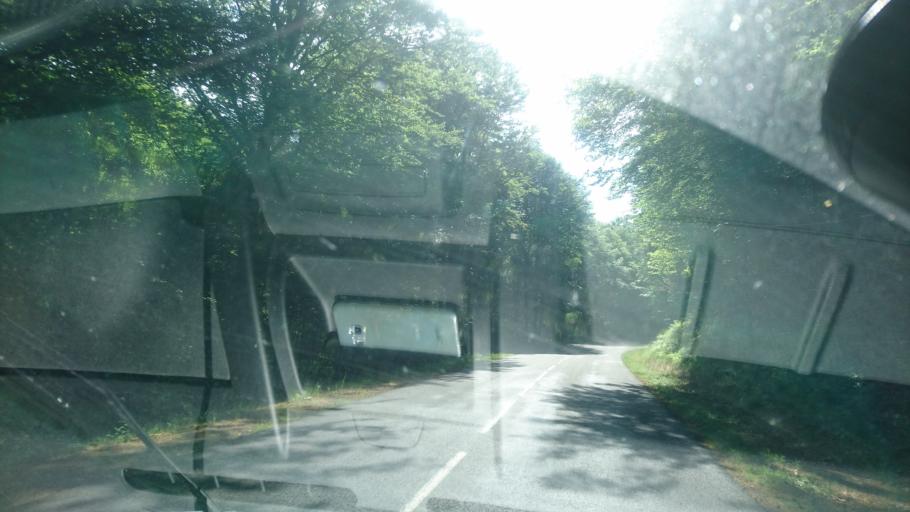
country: FR
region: Limousin
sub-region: Departement de la Haute-Vienne
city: Peyrat-le-Chateau
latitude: 45.8090
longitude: 1.8158
